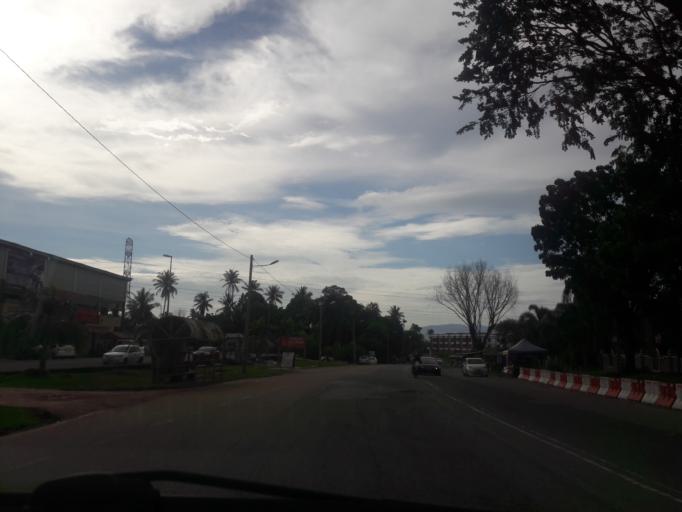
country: MY
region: Kedah
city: Sungai Petani
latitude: 5.6261
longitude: 100.5285
